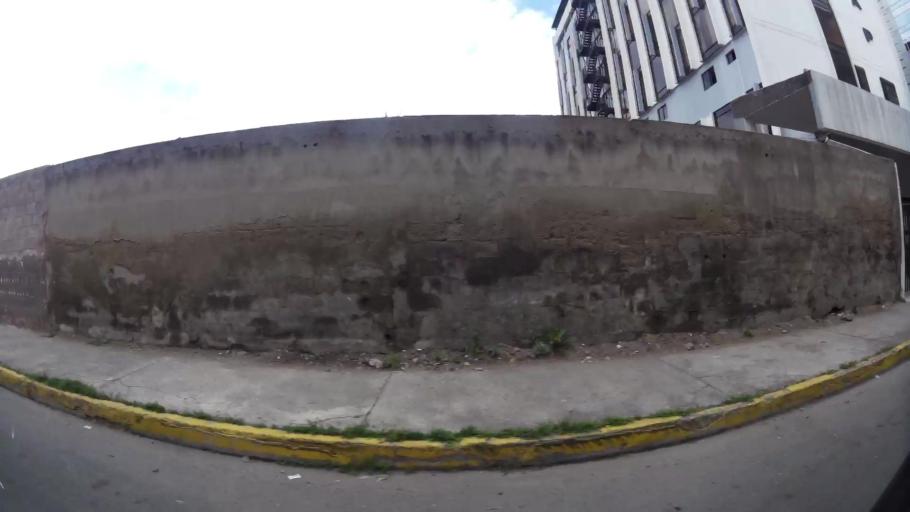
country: EC
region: Pichincha
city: Quito
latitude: -0.1706
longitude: -78.4855
